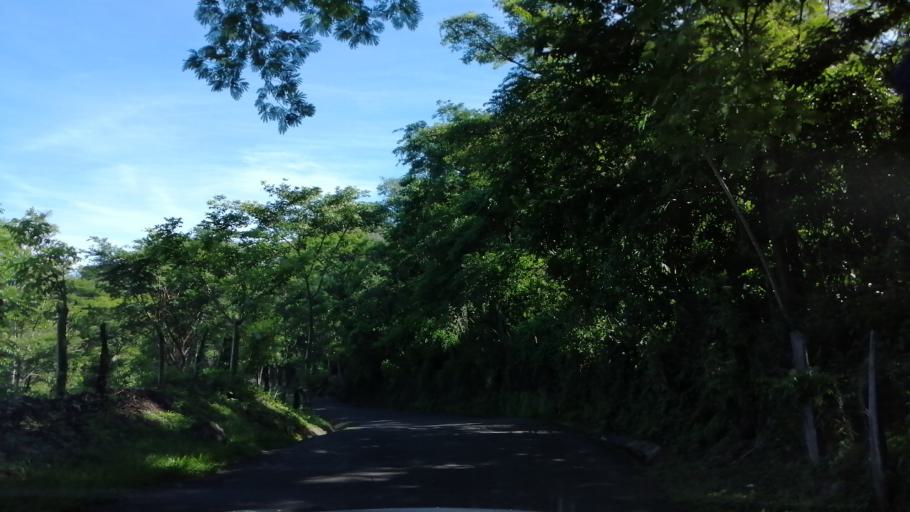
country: SV
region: Morazan
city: Corinto
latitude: 13.8028
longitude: -88.0039
